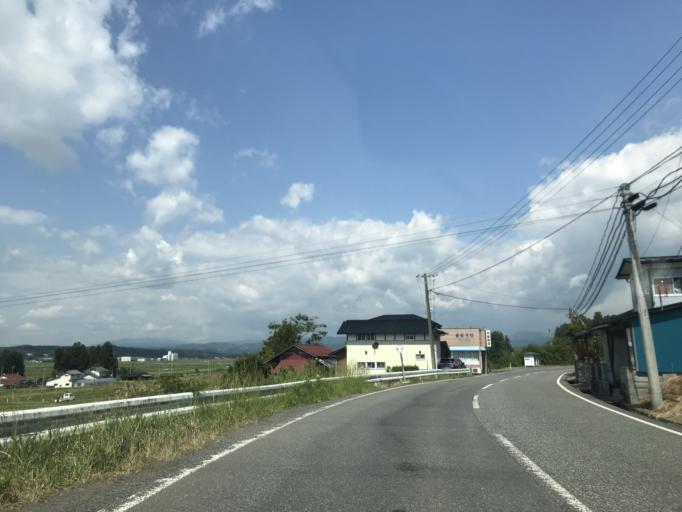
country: JP
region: Iwate
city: Ichinoseki
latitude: 38.8047
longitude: 141.0030
